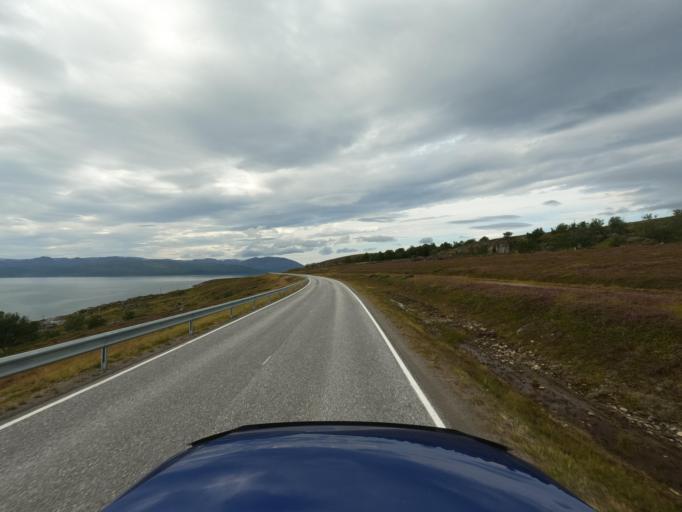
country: NO
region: Finnmark Fylke
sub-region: Kvalsund
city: Kvalsund
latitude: 70.5105
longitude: 23.8088
